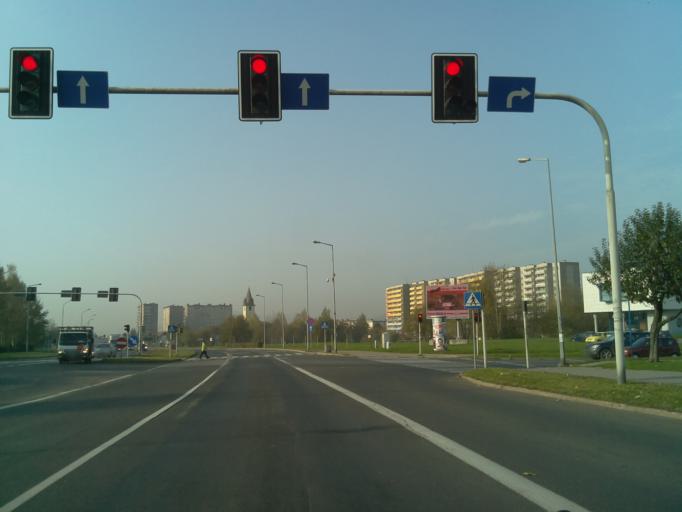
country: PL
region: Lower Silesian Voivodeship
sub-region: Powiat jeleniogorski
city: Jezow Sudecki
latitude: 50.9201
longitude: 15.7592
